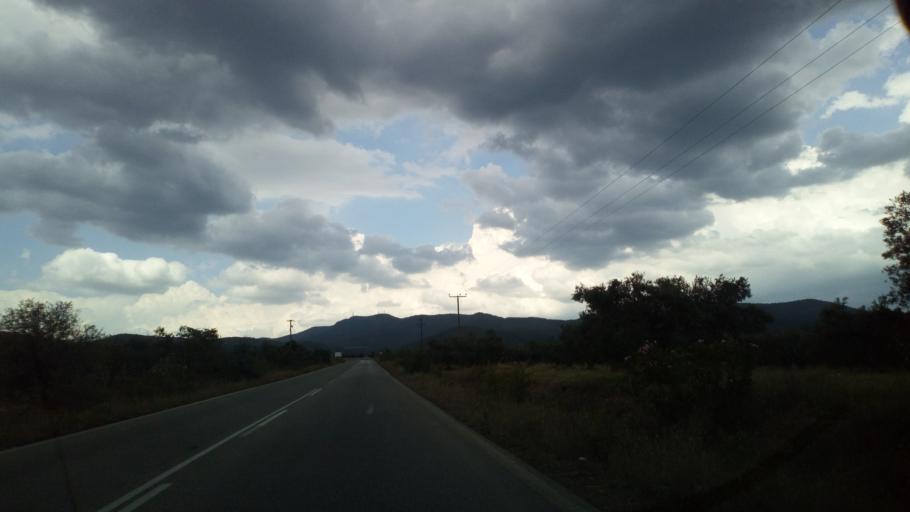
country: GR
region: Central Macedonia
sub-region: Nomos Chalkidikis
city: Polygyros
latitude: 40.3333
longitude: 23.4523
